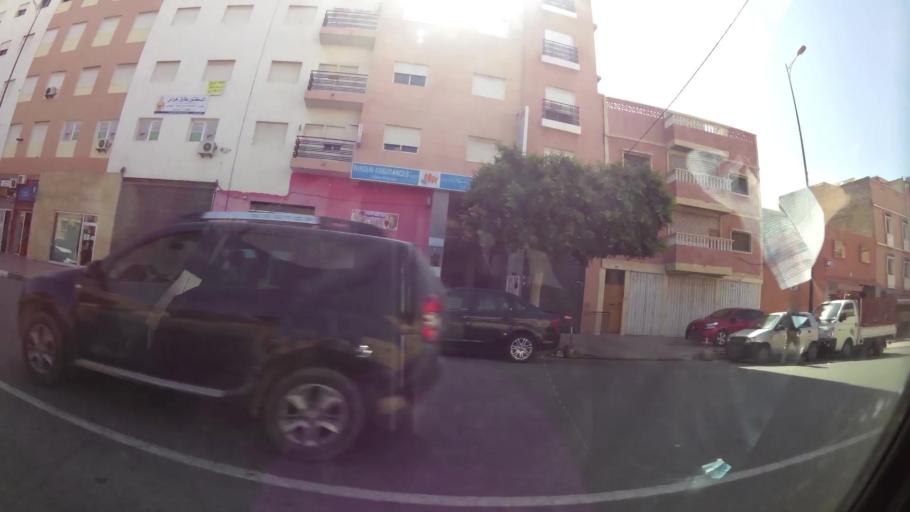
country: MA
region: Souss-Massa-Draa
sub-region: Inezgane-Ait Mellou
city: Inezgane
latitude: 30.3408
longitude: -9.5024
